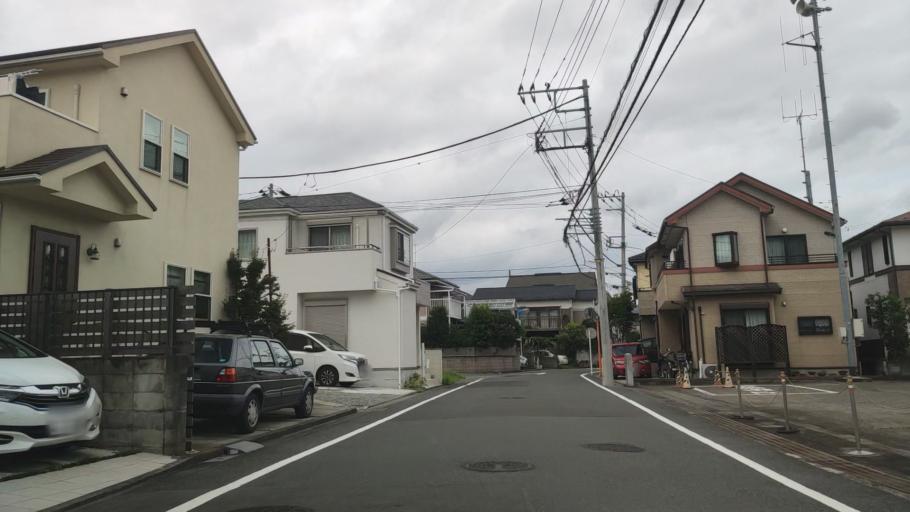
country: JP
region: Tokyo
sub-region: Machida-shi
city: Machida
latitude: 35.5131
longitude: 139.4369
